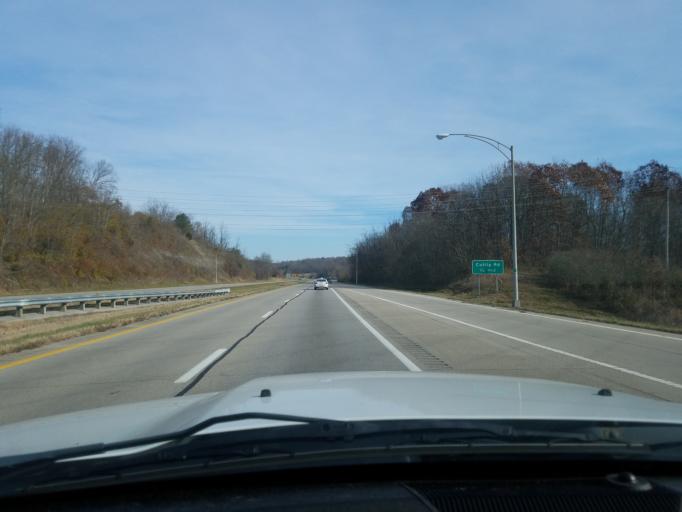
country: US
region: Ohio
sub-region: Jackson County
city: Jackson
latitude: 39.0473
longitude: -82.6086
